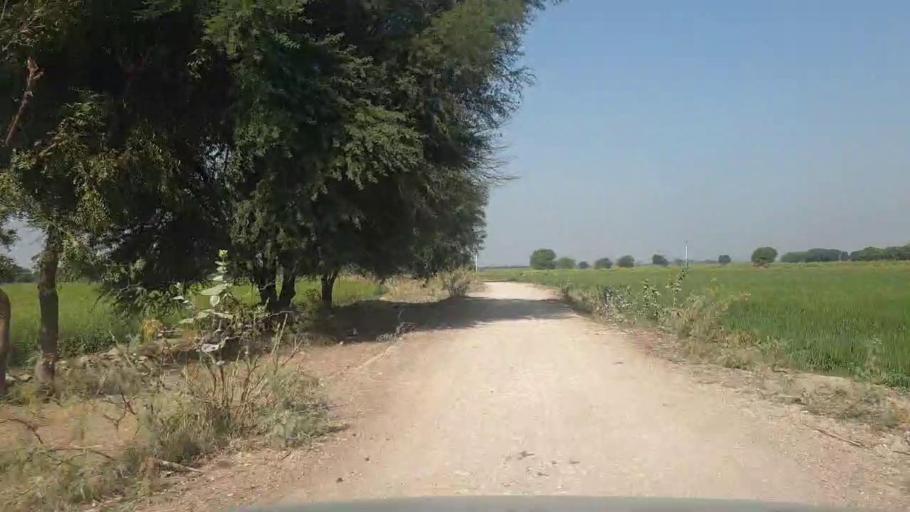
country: PK
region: Sindh
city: Chambar
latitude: 25.2492
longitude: 68.8239
